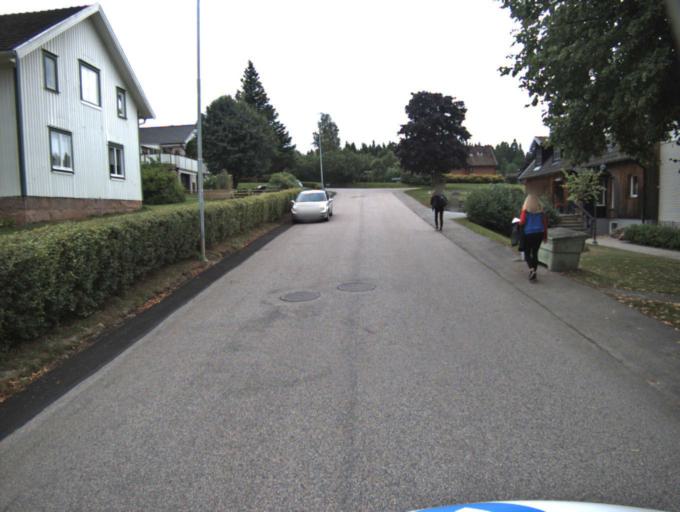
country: SE
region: Vaestra Goetaland
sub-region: Ulricehamns Kommun
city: Ulricehamn
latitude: 57.8371
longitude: 13.2830
